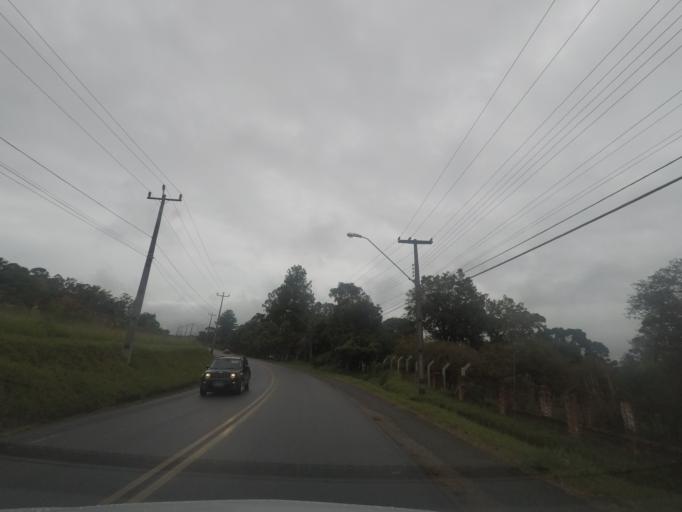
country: BR
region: Parana
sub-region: Campina Grande Do Sul
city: Campina Grande do Sul
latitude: -25.3242
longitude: -49.0784
